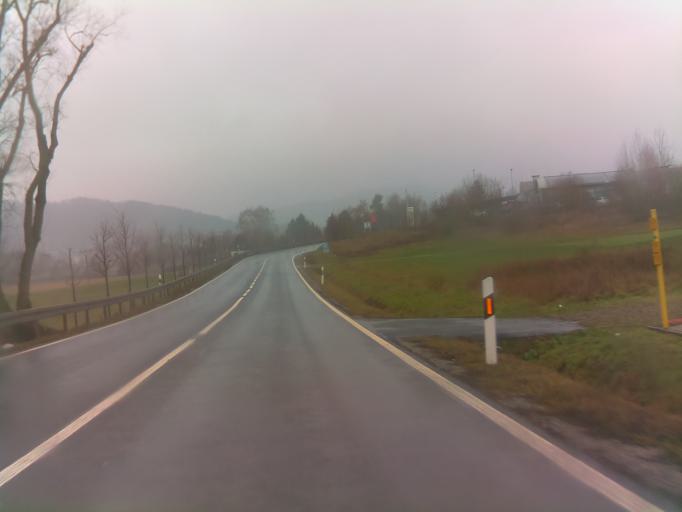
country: DE
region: Thuringia
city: Hildburghausen
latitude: 50.4199
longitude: 10.7561
